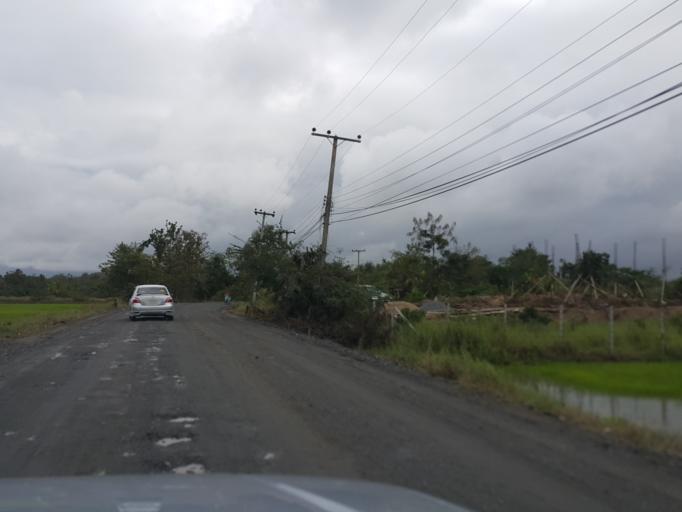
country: TH
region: Chiang Mai
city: San Kamphaeng
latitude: 18.6984
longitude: 99.1068
